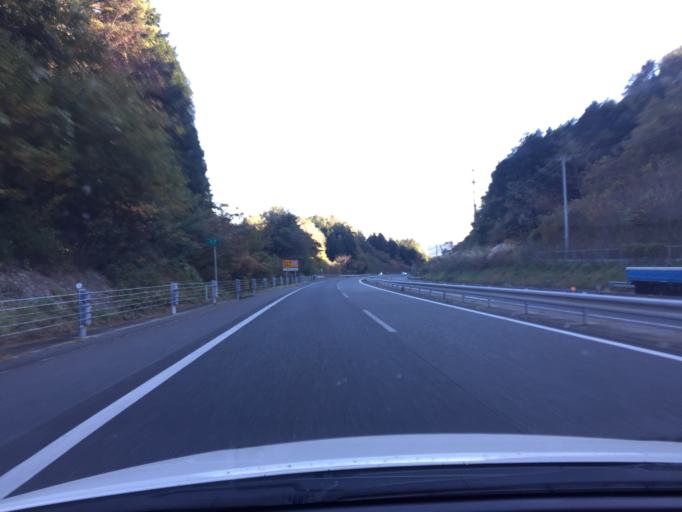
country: JP
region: Fukushima
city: Iwaki
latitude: 37.1636
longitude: 140.7294
